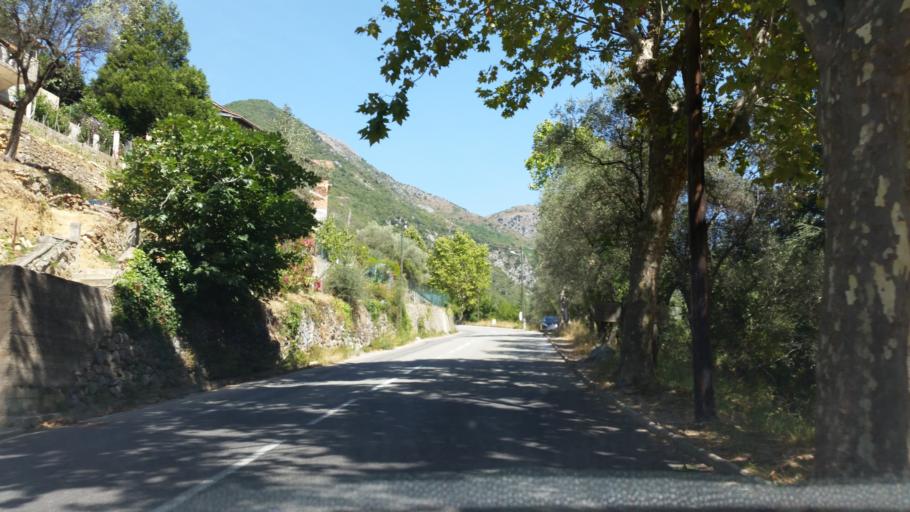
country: FR
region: Provence-Alpes-Cote d'Azur
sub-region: Departement des Alpes-Maritimes
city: Breil-sur-Roya
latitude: 43.9502
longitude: 7.5174
